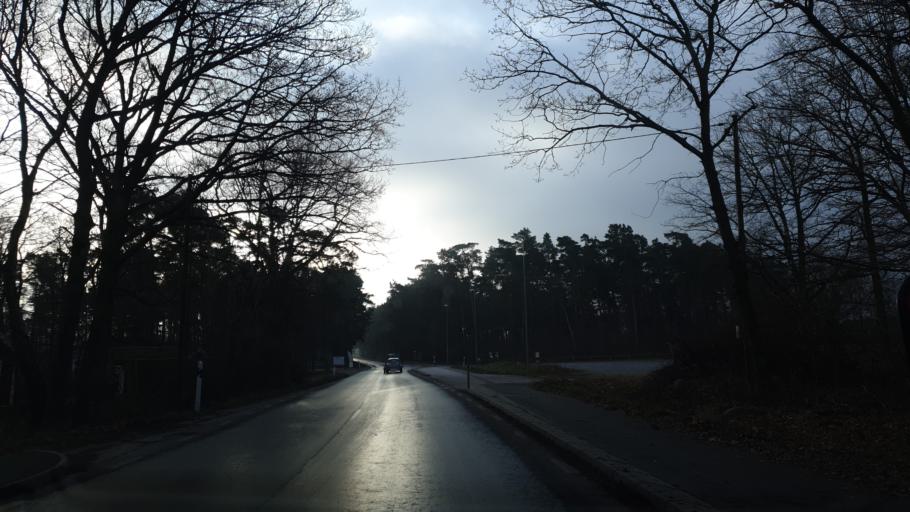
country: SE
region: Blekinge
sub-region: Karlshamns Kommun
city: Morrum
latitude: 56.1268
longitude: 14.6735
